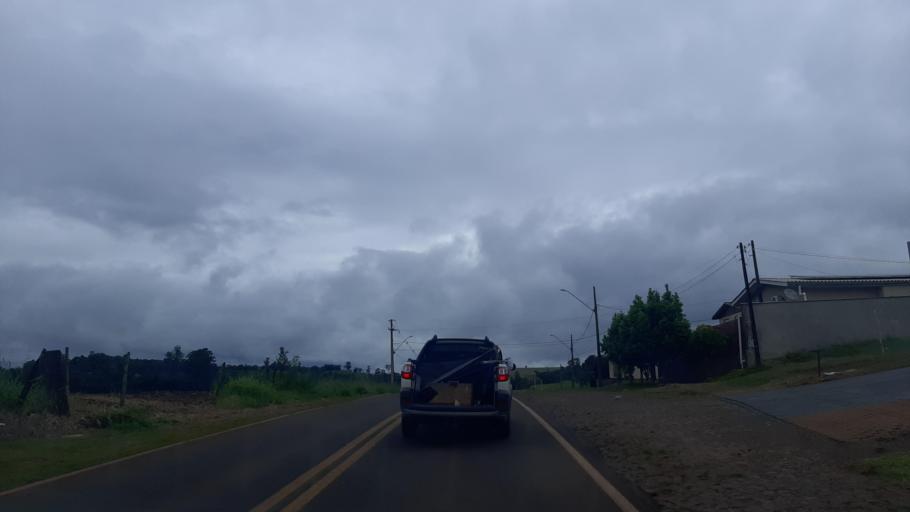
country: BR
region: Parana
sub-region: Ampere
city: Ampere
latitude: -25.9305
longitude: -53.4661
